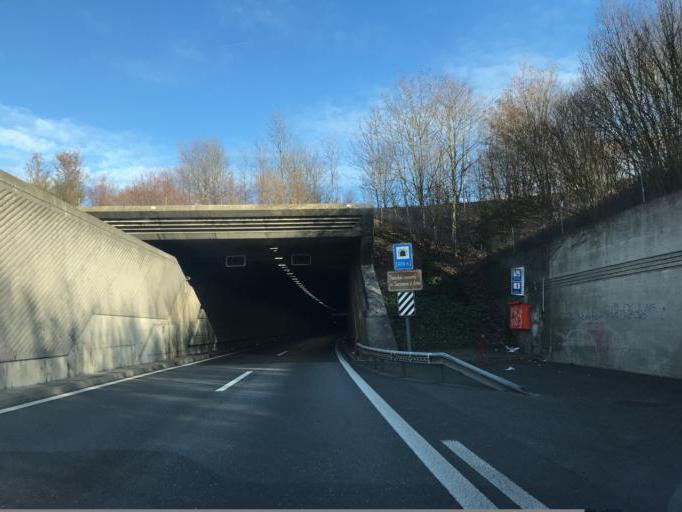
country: CH
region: Geneva
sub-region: Geneva
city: Plan-les-Ouates
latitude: 46.1630
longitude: 6.1207
